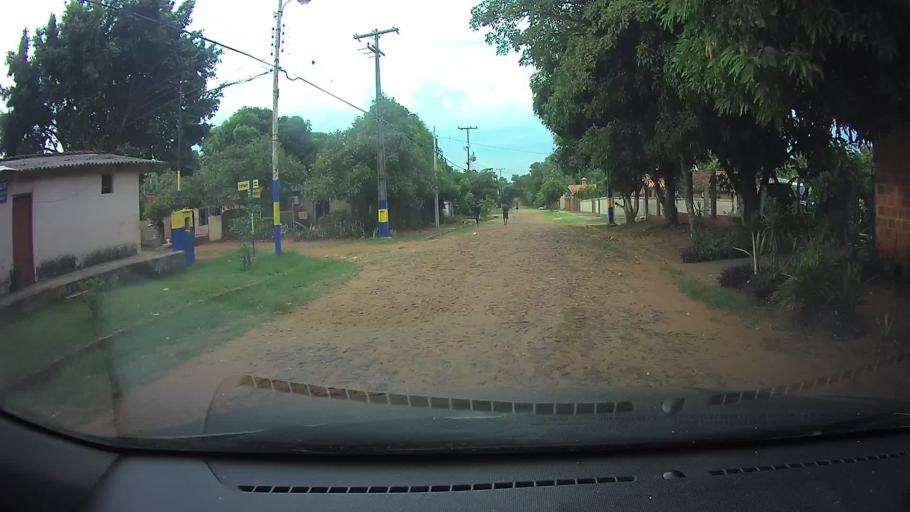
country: PY
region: Central
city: San Lorenzo
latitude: -25.2611
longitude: -57.4633
